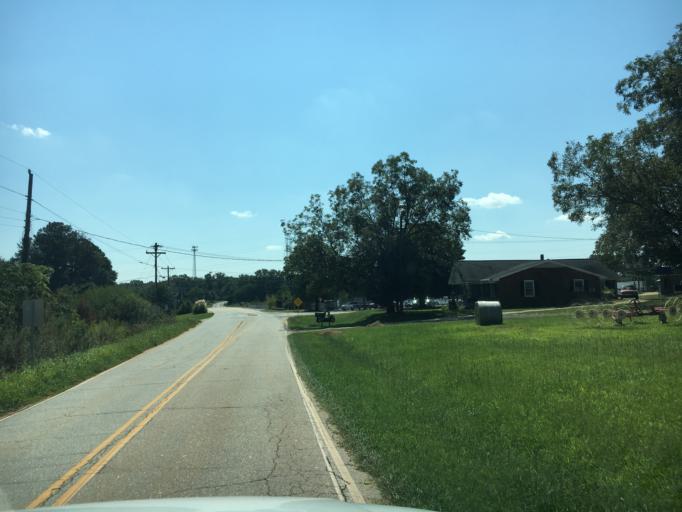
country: US
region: South Carolina
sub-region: Spartanburg County
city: Valley Falls
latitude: 35.0139
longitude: -81.9292
